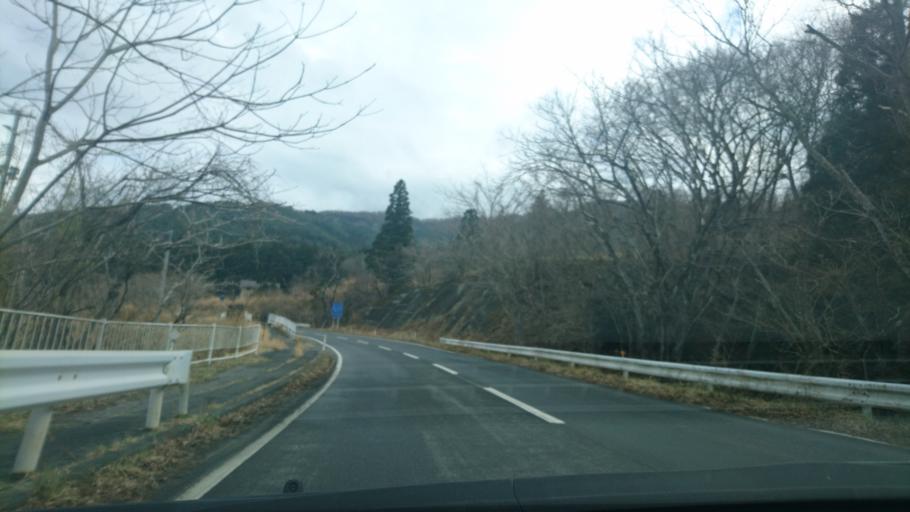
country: JP
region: Iwate
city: Ofunato
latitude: 39.1410
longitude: 141.8231
